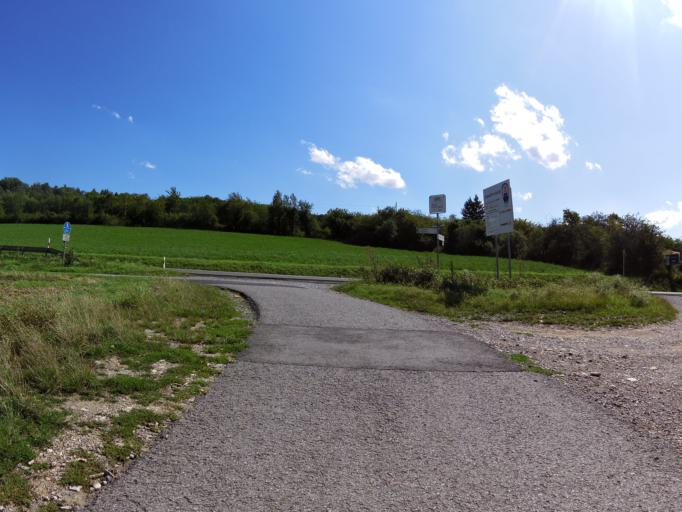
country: DE
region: Bavaria
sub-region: Regierungsbezirk Unterfranken
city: Frickenhausen
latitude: 49.6675
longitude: 10.0921
